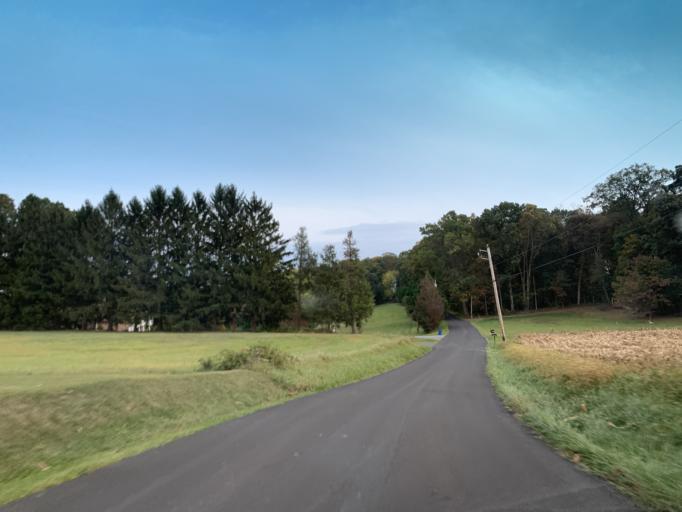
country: US
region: Pennsylvania
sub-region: York County
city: Stewartstown
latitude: 39.6797
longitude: -76.6360
